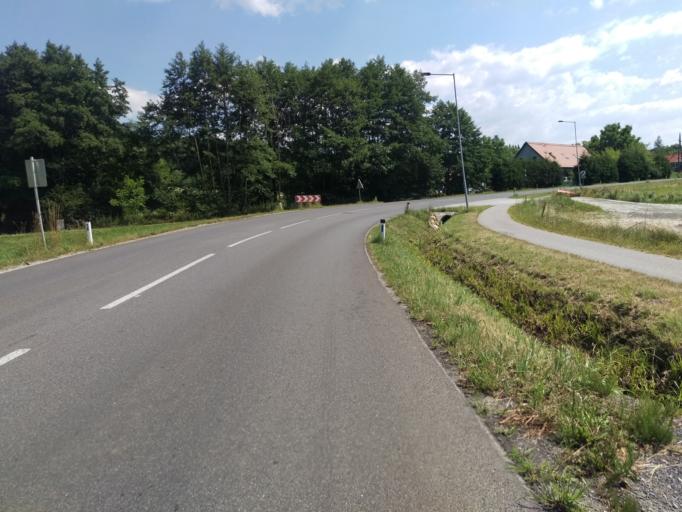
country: AT
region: Styria
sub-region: Politischer Bezirk Graz-Umgebung
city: Sankt Radegund bei Graz
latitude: 47.1428
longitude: 15.4968
